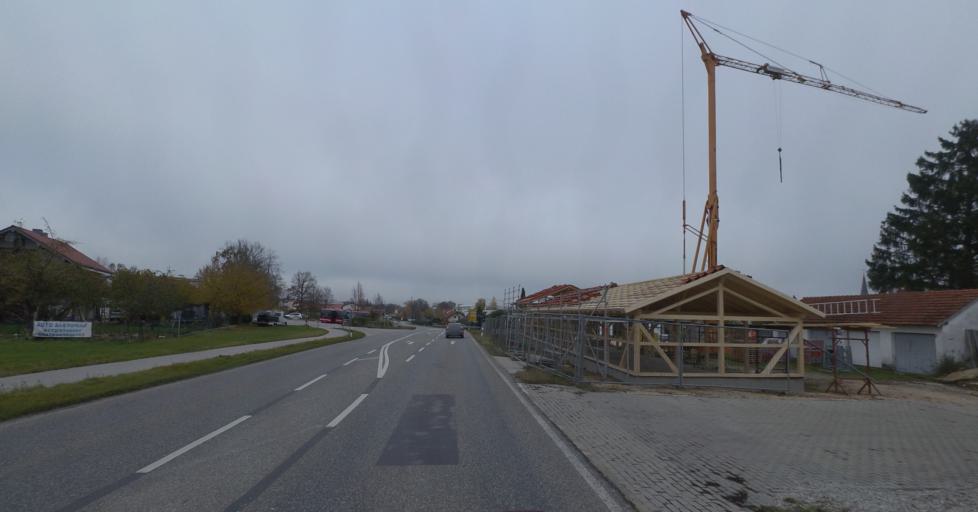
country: DE
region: Bavaria
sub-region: Upper Bavaria
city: Tacherting
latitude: 48.0551
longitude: 12.5693
